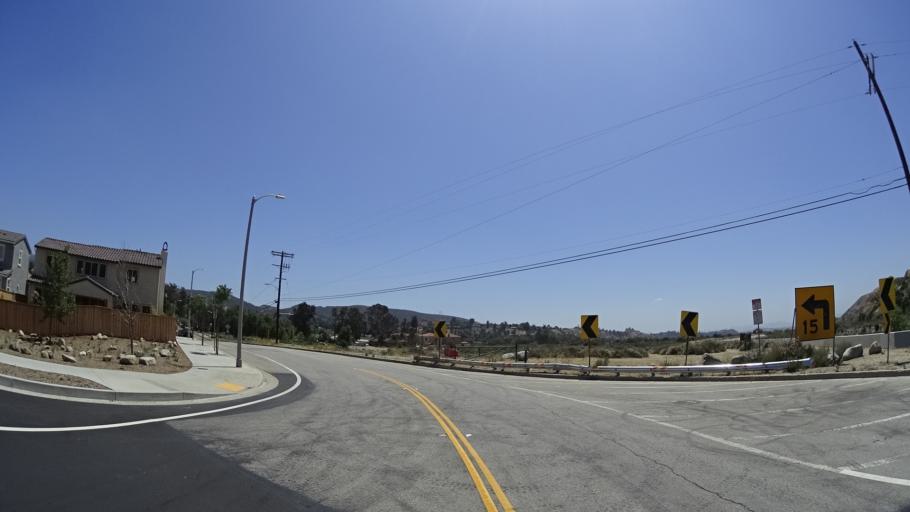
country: US
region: California
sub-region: Los Angeles County
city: La Crescenta-Montrose
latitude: 34.2725
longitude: -118.3156
